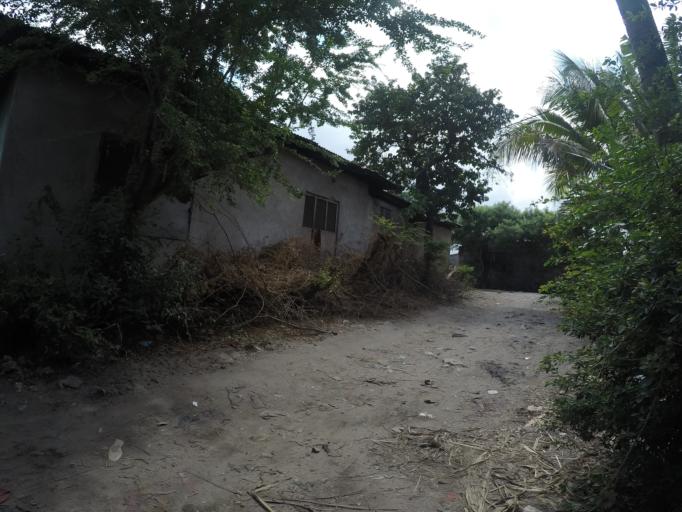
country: TZ
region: Zanzibar Urban/West
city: Zanzibar
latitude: -6.1785
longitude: 39.2119
